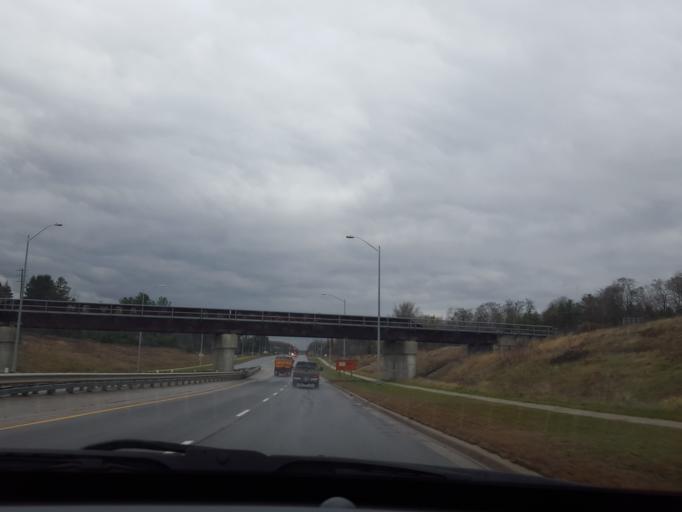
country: CA
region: Ontario
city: Pickering
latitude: 43.8825
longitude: -79.0889
